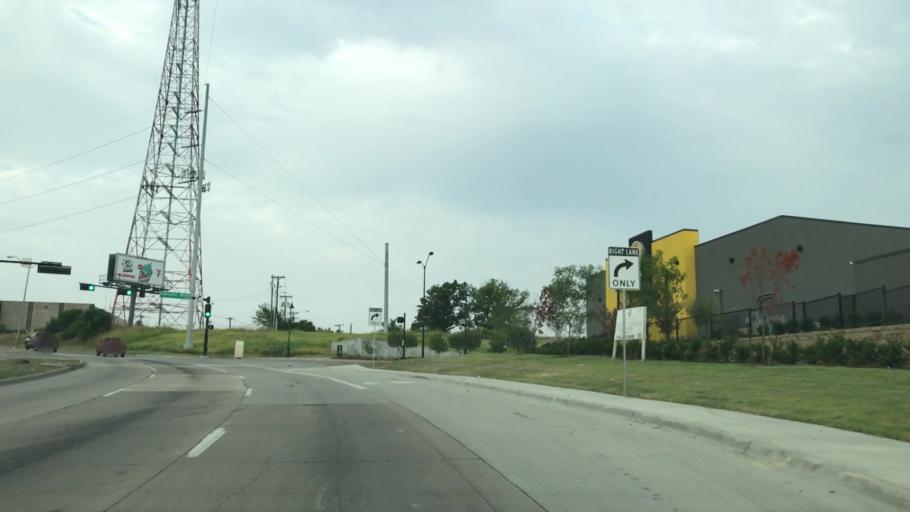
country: US
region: Texas
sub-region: Dallas County
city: Cockrell Hill
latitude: 32.7663
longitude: -96.8740
